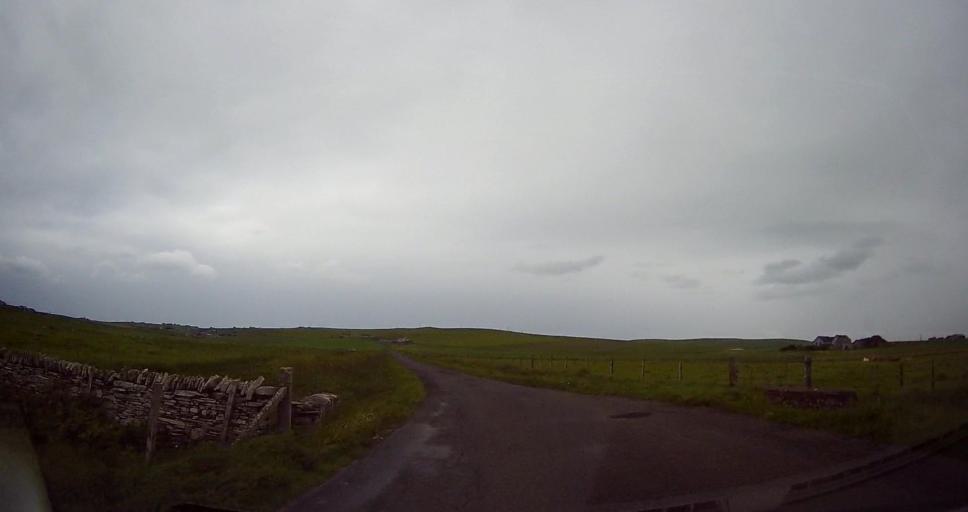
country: GB
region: Scotland
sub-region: Orkney Islands
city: Stromness
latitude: 59.0695
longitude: -3.2832
